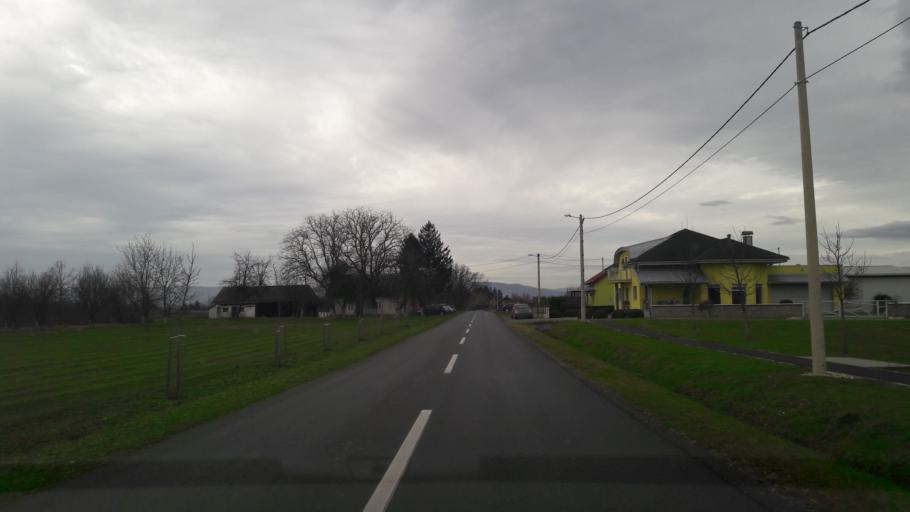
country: HR
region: Osjecko-Baranjska
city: Martin
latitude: 45.5324
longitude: 18.0588
